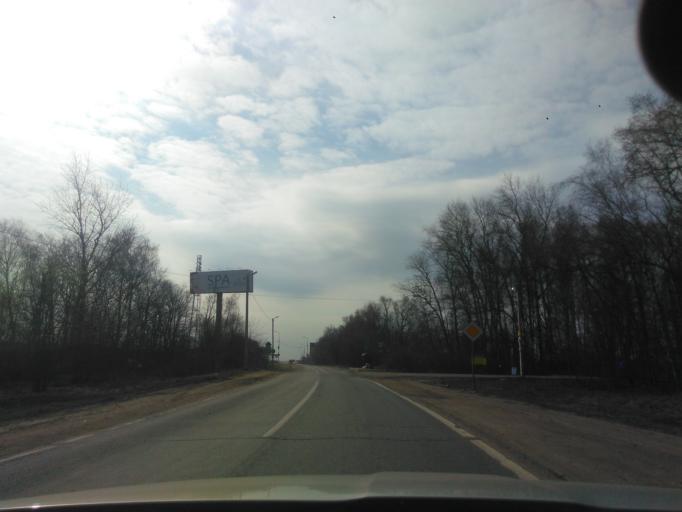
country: RU
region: Moskovskaya
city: Nekrasovskiy
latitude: 56.0687
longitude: 37.5158
